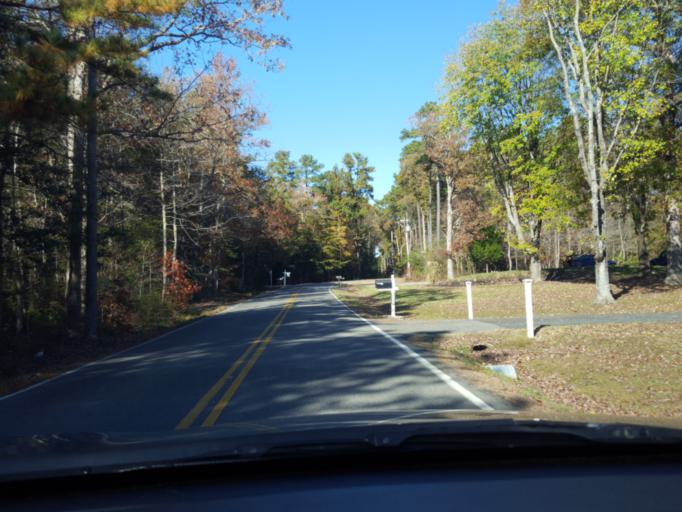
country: US
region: Maryland
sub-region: Saint Mary's County
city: California
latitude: 38.2423
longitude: -76.5434
